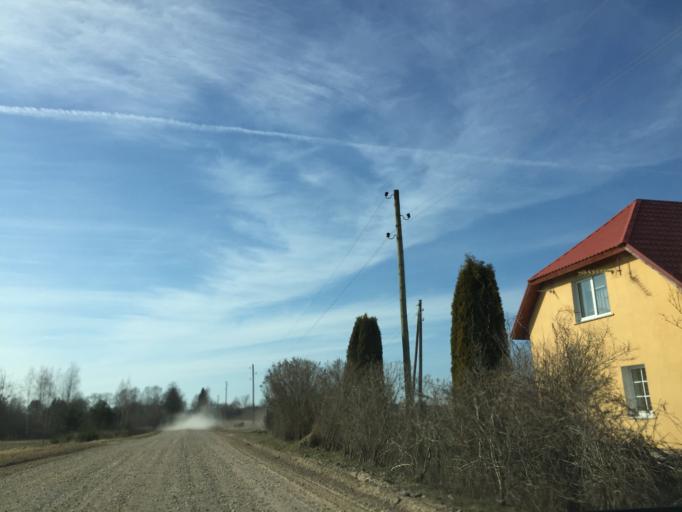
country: LV
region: Saulkrastu
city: Saulkrasti
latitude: 57.2849
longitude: 24.4952
